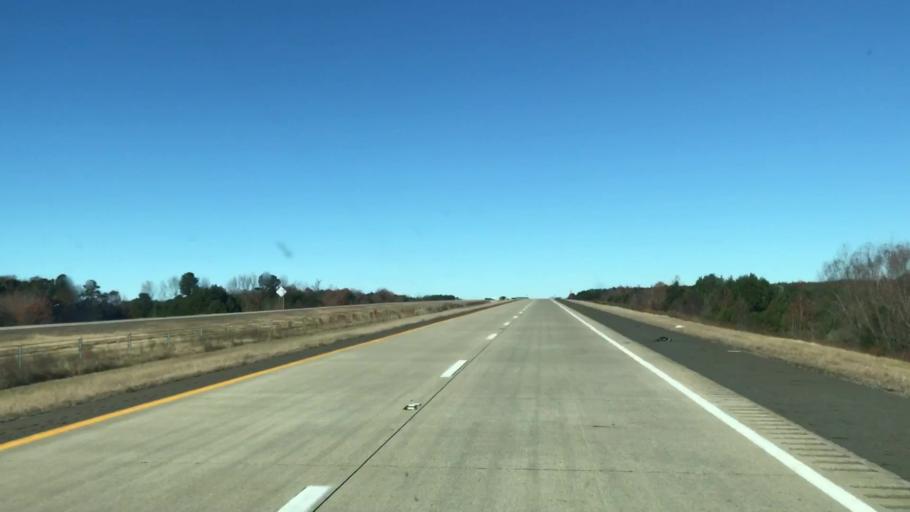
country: US
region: Texas
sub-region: Bowie County
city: Texarkana
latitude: 33.2479
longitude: -93.8823
